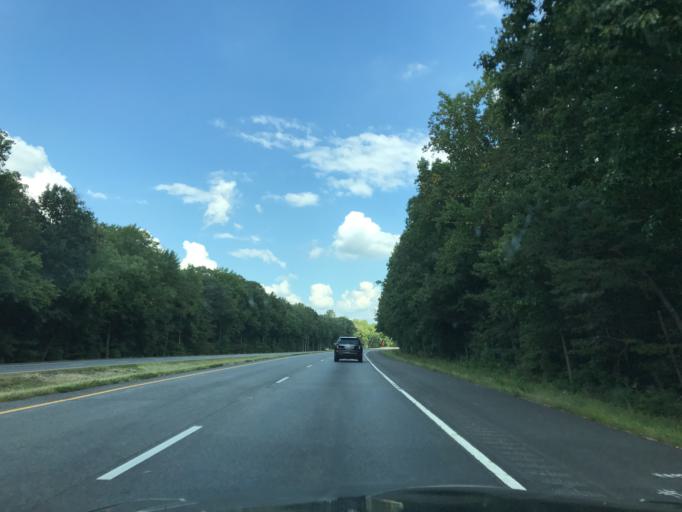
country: US
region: Maryland
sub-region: Queen Anne's County
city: Kingstown
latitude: 39.1871
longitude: -75.9144
